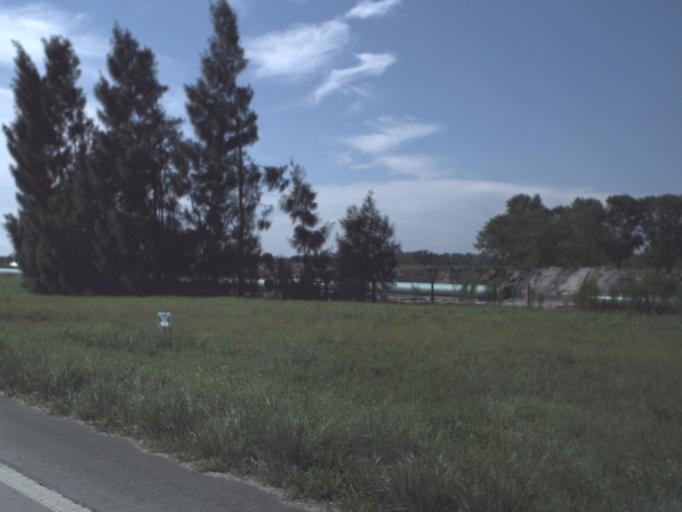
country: US
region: Florida
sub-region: Indian River County
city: Fellsmere
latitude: 27.6416
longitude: -80.8745
